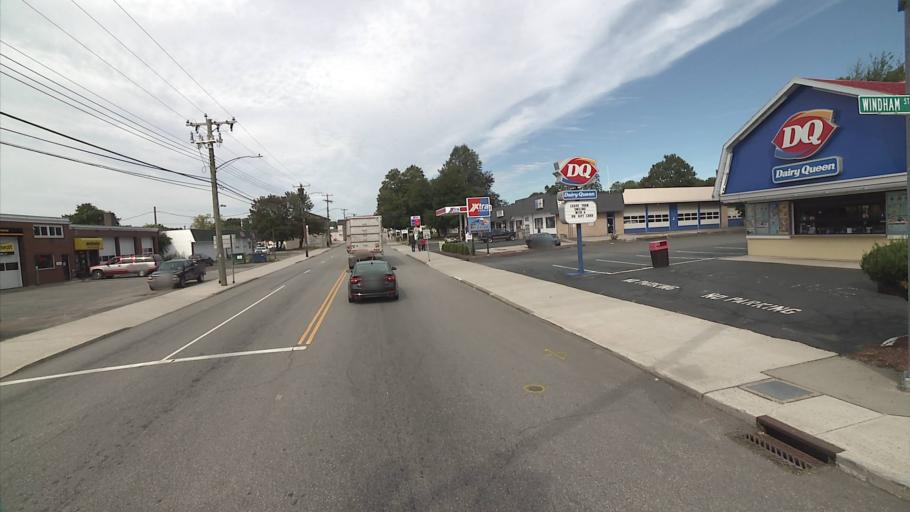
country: US
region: Connecticut
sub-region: Windham County
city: Willimantic
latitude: 41.7132
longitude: -72.2197
